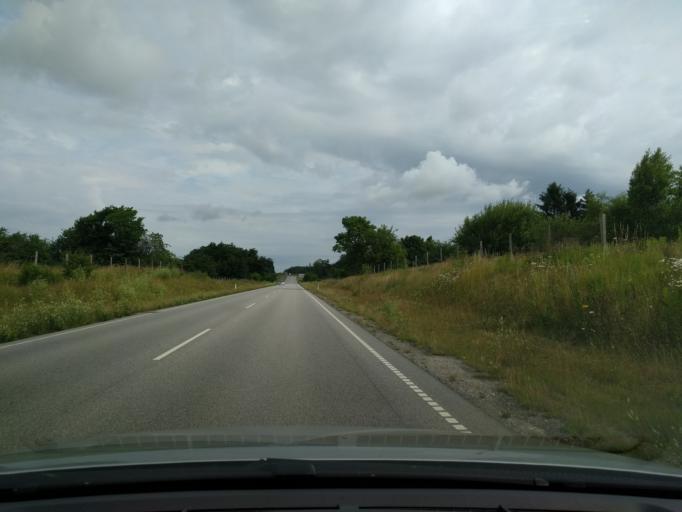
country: DK
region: Zealand
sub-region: Naestved Kommune
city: Naestved
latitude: 55.2268
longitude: 11.7981
